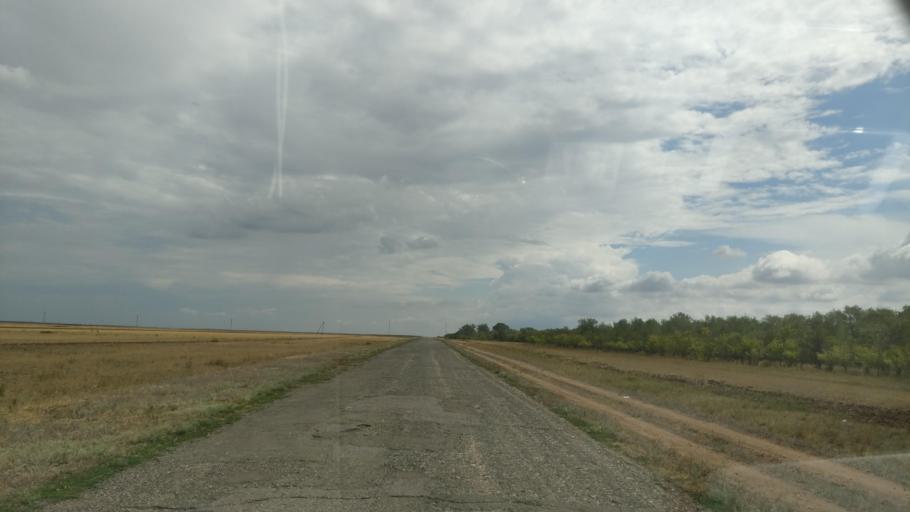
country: KZ
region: Pavlodar
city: Pavlodar
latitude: 52.6437
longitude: 77.0403
